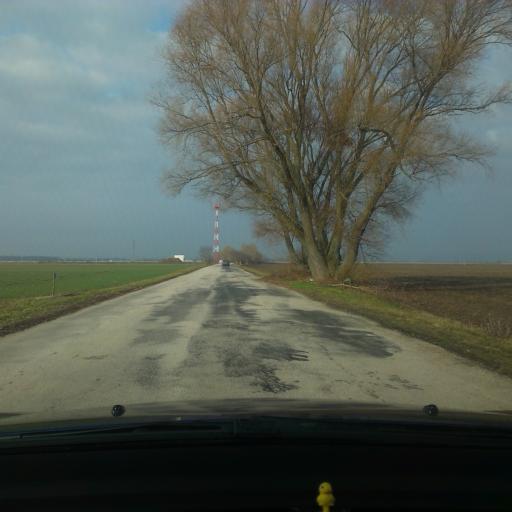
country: SK
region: Trnavsky
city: Leopoldov
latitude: 48.5179
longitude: 17.7960
